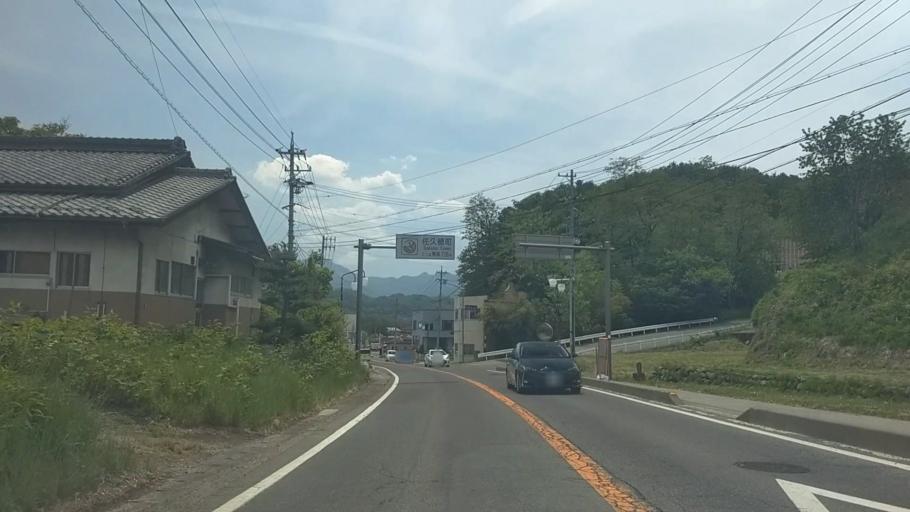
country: JP
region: Nagano
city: Saku
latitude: 36.1798
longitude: 138.4822
